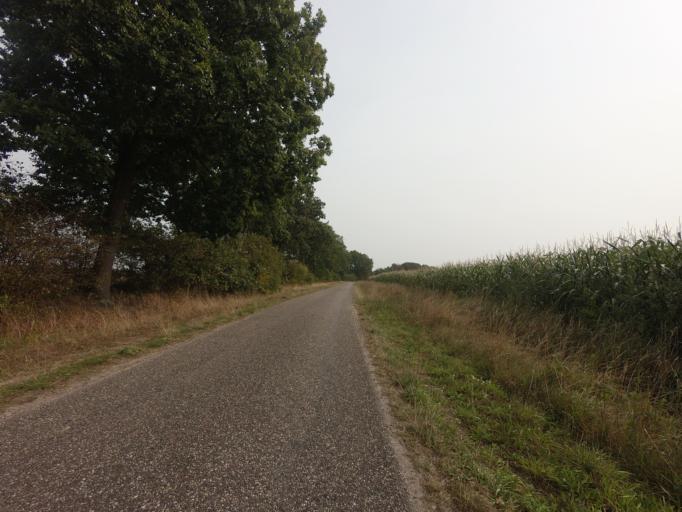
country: NL
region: Drenthe
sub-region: Gemeente Tynaarlo
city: Vries
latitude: 53.1148
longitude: 6.5408
